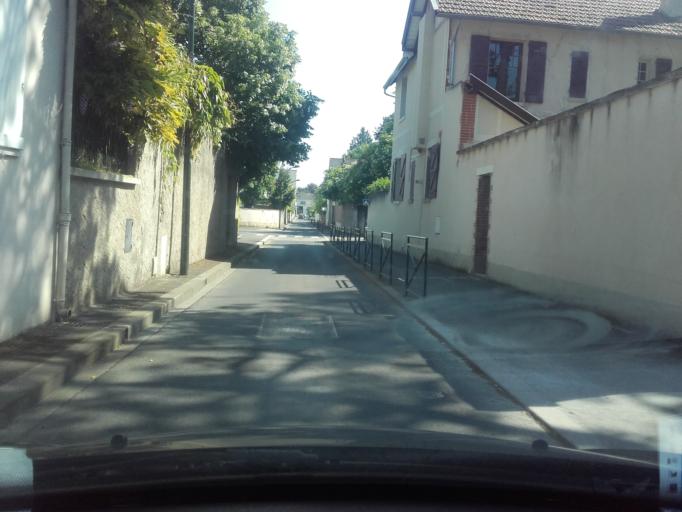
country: FR
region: Centre
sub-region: Departement d'Indre-et-Loire
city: Saint-Cyr-sur-Loire
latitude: 47.4136
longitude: 0.6758
